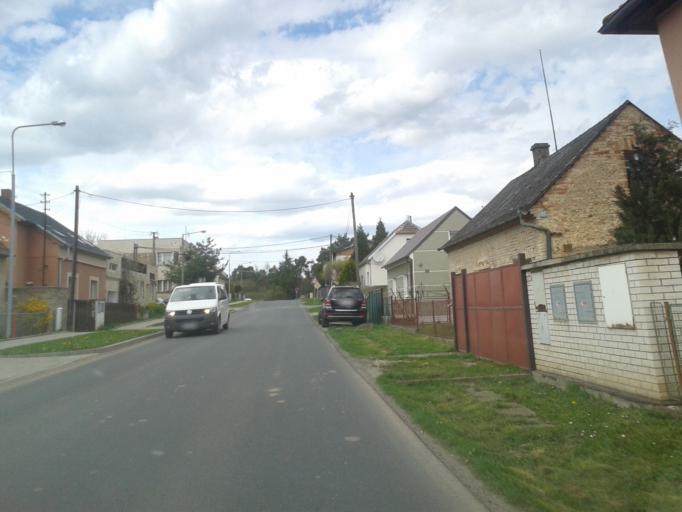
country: CZ
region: Central Bohemia
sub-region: Okres Beroun
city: Lodenice
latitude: 50.0065
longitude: 14.1522
